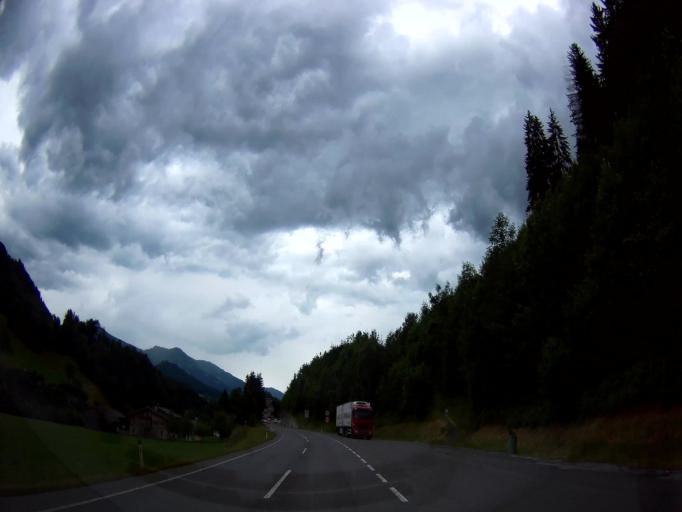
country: AT
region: Salzburg
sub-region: Politischer Bezirk Sankt Johann im Pongau
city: Pfarrwerfen
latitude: 47.4486
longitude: 13.2099
